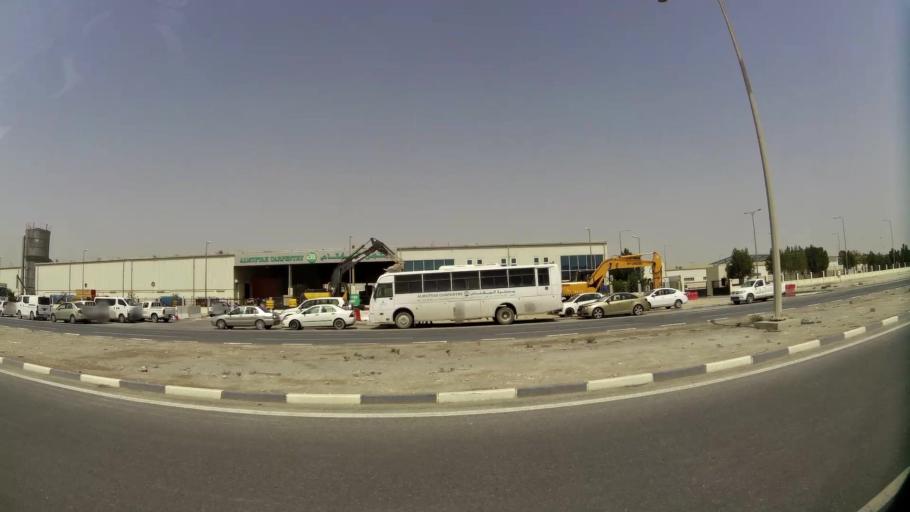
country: QA
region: Al Wakrah
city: Al Wukayr
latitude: 25.1580
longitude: 51.4070
